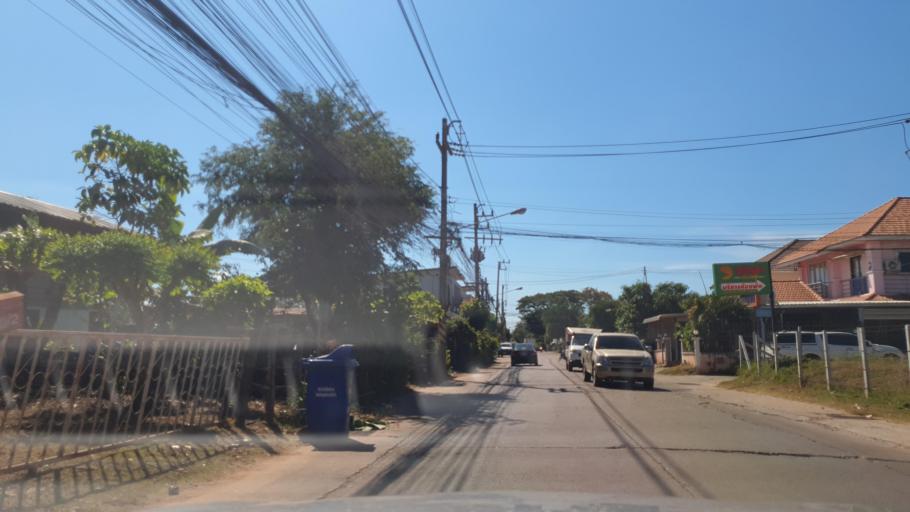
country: TH
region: Sakon Nakhon
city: Sakon Nakhon
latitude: 17.1590
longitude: 104.1216
